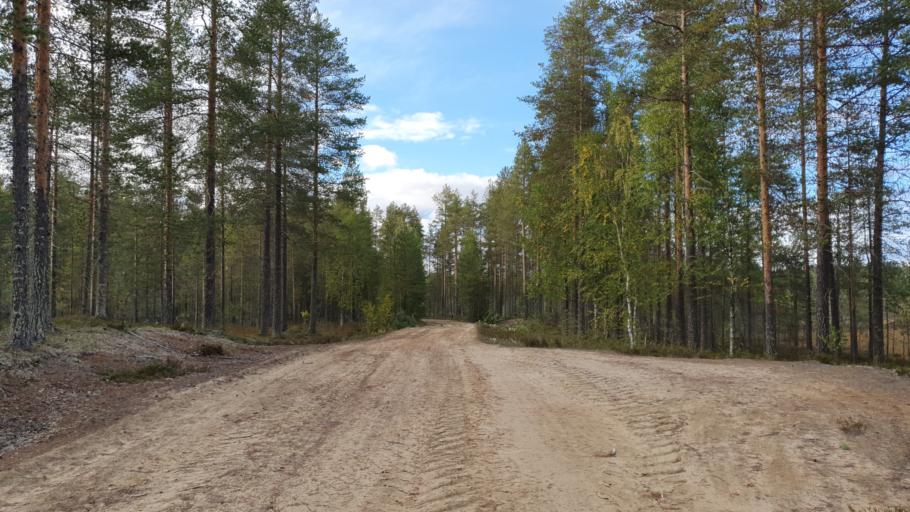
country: FI
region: Kainuu
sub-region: Kehys-Kainuu
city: Kuhmo
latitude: 64.2023
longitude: 29.1676
